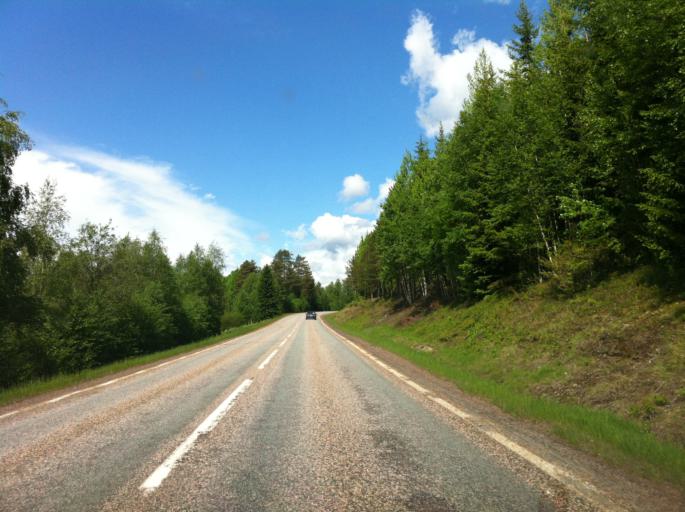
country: SE
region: Dalarna
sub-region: Malung-Saelens kommun
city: Malung
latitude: 61.0410
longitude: 13.3367
